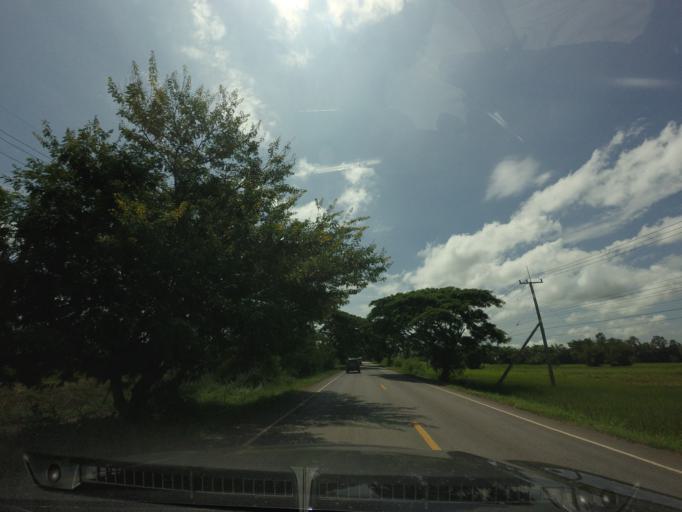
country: TH
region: Changwat Udon Thani
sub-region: Amphoe Ban Phue
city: Ban Phue
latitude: 17.7589
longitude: 102.3977
